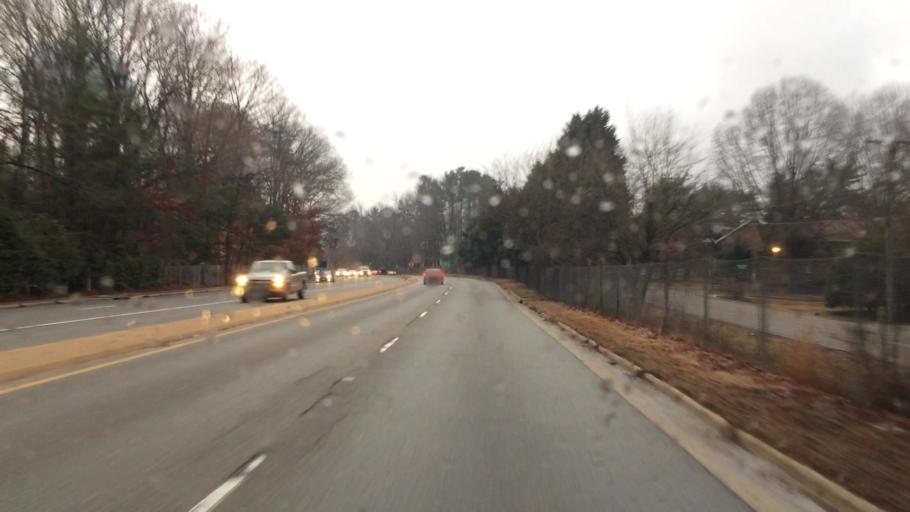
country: US
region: Virginia
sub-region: James City County
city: Williamsburg
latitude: 37.2532
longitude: -76.7307
